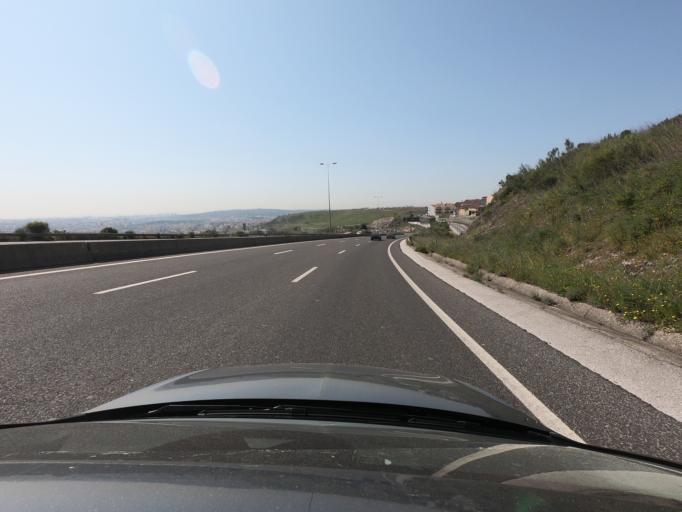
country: PT
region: Lisbon
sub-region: Odivelas
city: Famoes
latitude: 38.7828
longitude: -9.2294
